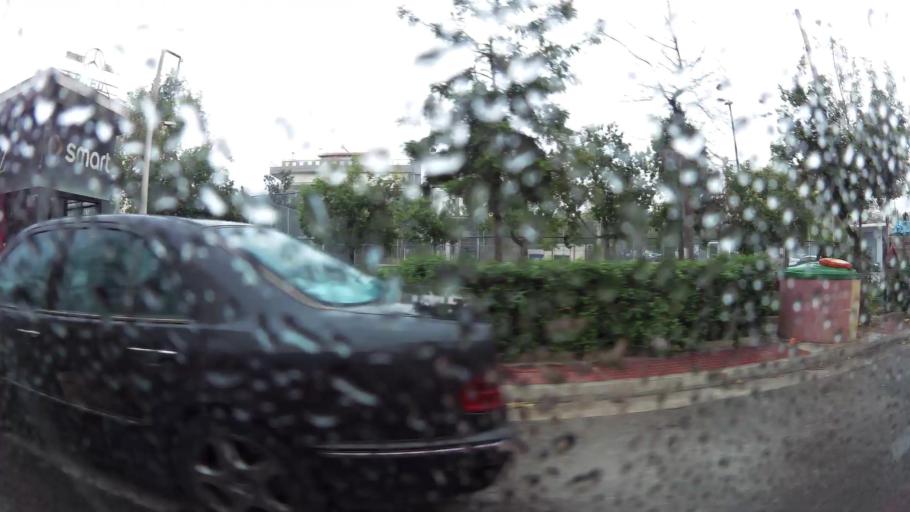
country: GR
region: Attica
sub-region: Nomarchia Athinas
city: Agioi Anargyroi
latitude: 38.0181
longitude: 23.7193
